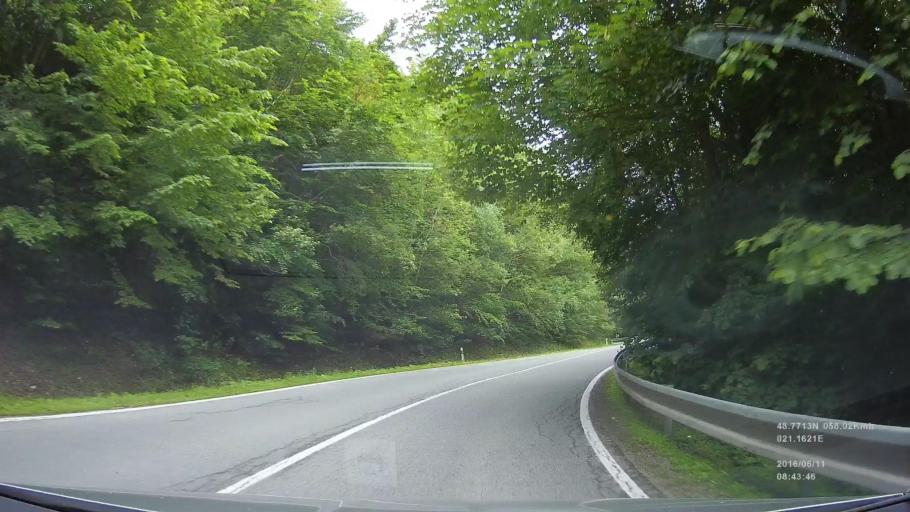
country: SK
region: Kosicky
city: Kosice
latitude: 48.7558
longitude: 21.1940
